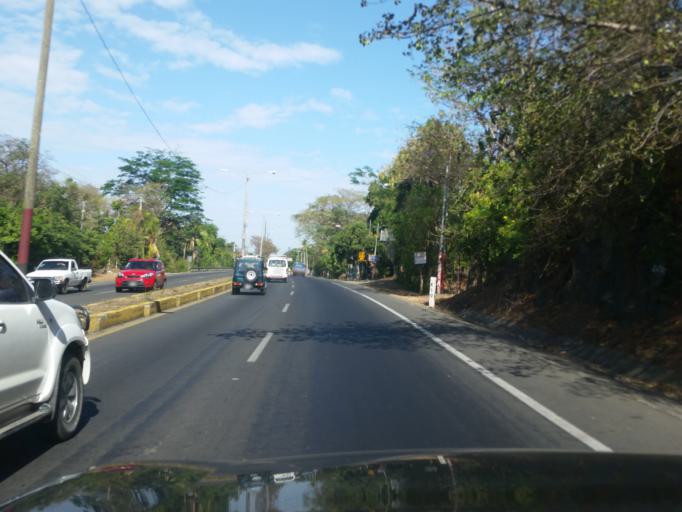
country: NI
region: Masaya
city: Ticuantepe
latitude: 12.0256
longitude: -86.1743
